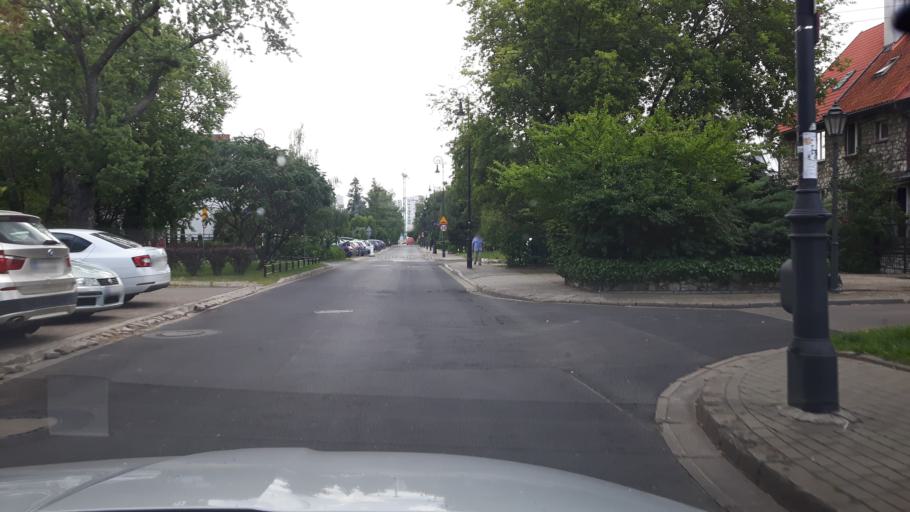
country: PL
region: Masovian Voivodeship
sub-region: Warszawa
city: Mokotow
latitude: 52.1805
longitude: 21.0619
